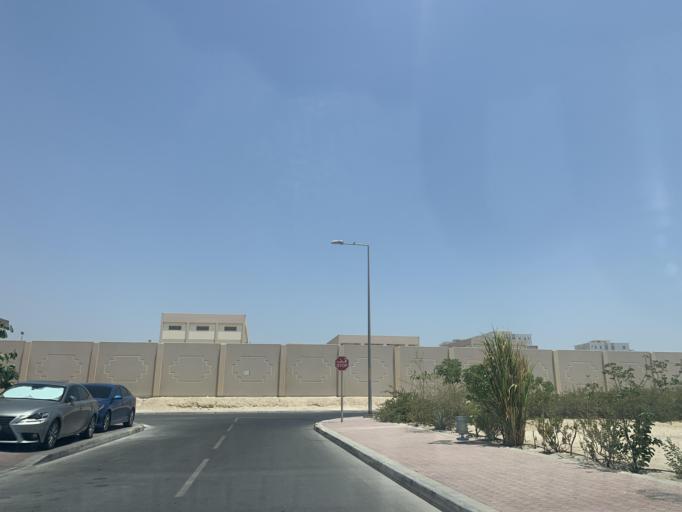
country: BH
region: Manama
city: Jidd Hafs
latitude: 26.2342
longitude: 50.4639
